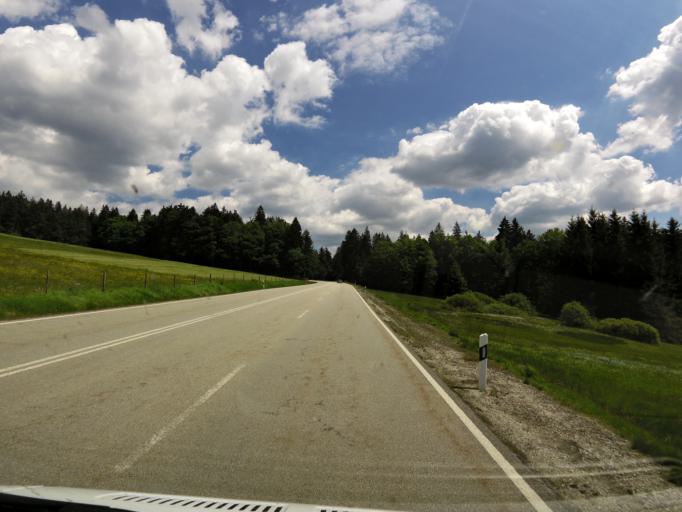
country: DE
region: Bavaria
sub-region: Lower Bavaria
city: Philippsreut
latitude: 48.8463
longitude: 13.6674
